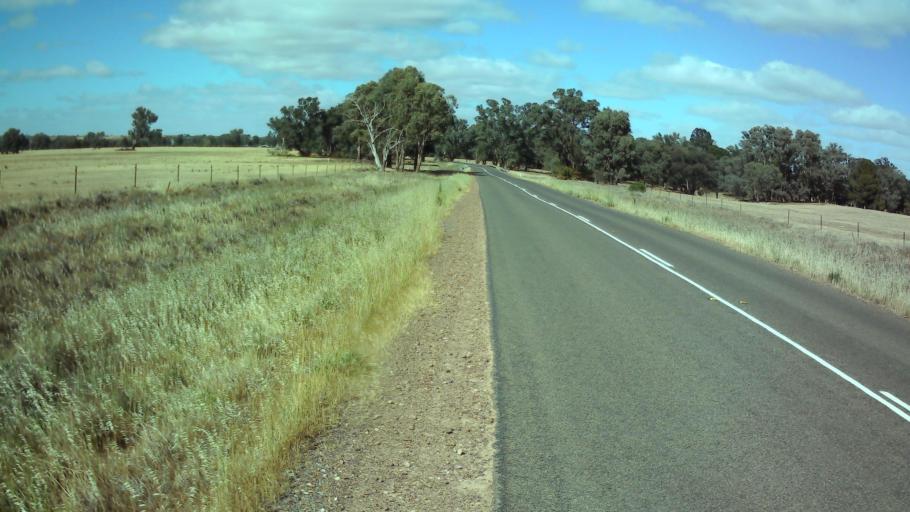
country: AU
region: New South Wales
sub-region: Weddin
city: Grenfell
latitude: -33.9877
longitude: 148.4114
